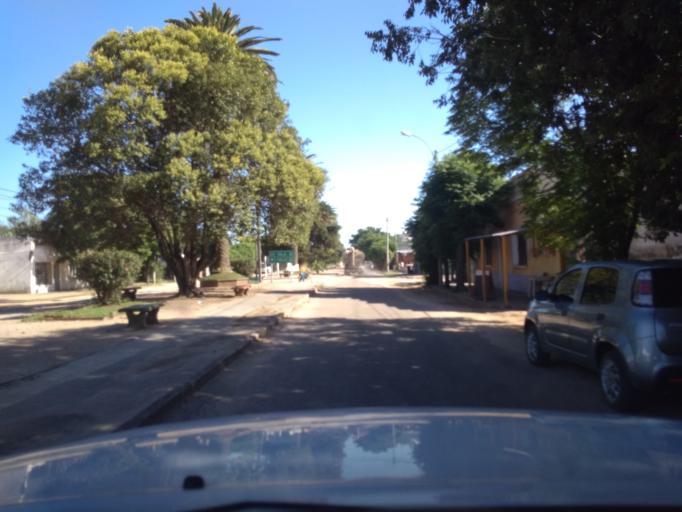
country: UY
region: Canelones
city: San Ramon
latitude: -34.2982
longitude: -55.9577
